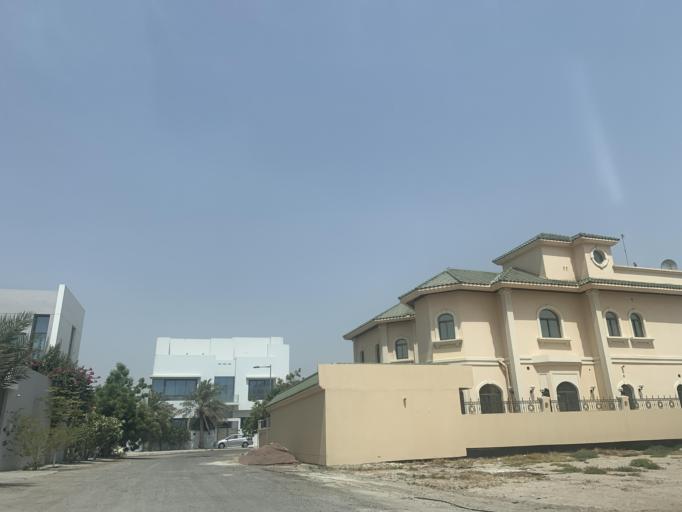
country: BH
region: Manama
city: Jidd Hafs
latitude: 26.1999
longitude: 50.5046
